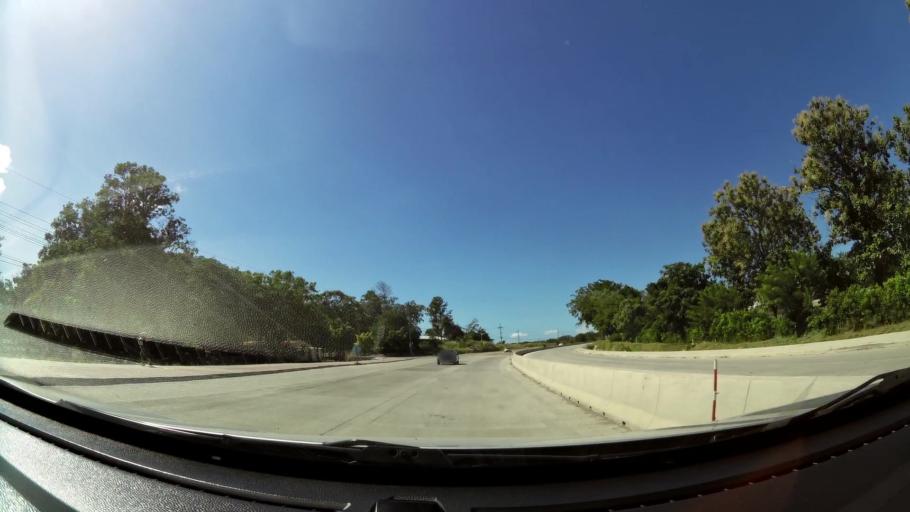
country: CR
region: Guanacaste
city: Liberia
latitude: 10.5515
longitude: -85.3678
